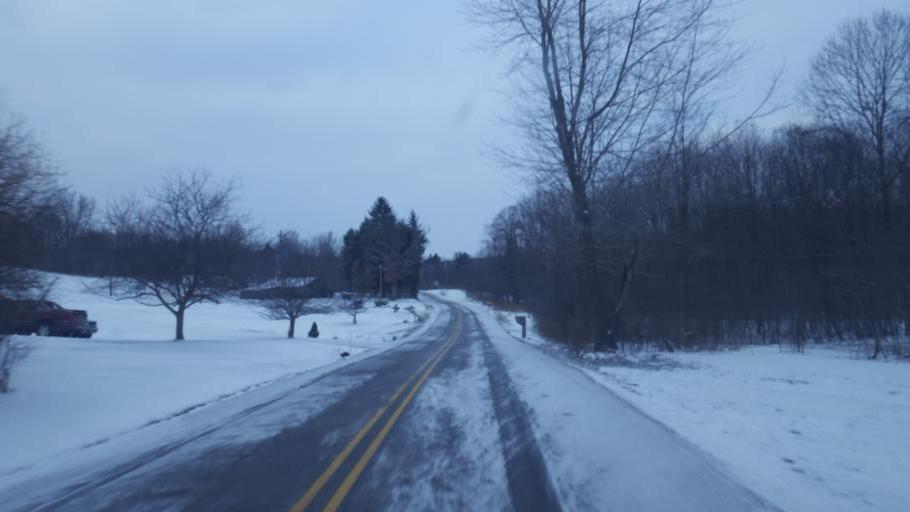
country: US
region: Pennsylvania
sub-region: Venango County
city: Sugarcreek
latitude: 41.4183
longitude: -79.9896
